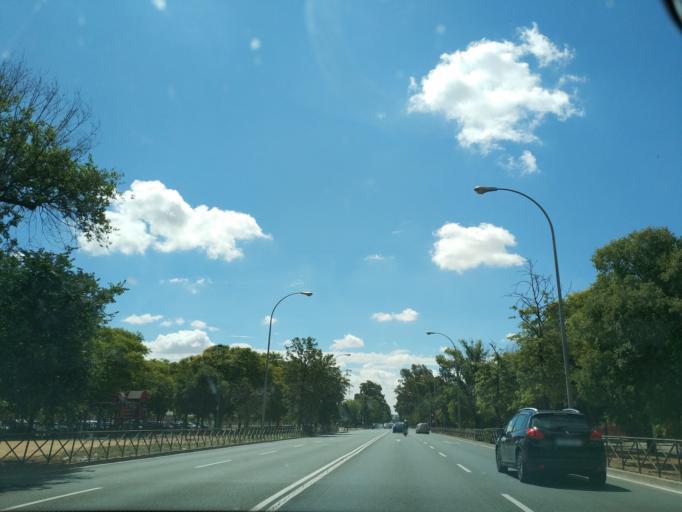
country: ES
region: Andalusia
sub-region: Provincia de Sevilla
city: Sevilla
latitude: 37.3661
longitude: -5.9652
